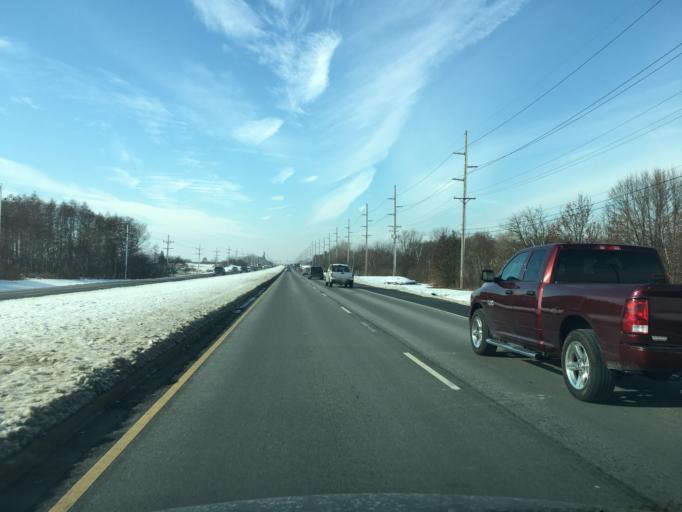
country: US
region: Illinois
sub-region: DuPage County
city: Naperville
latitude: 41.7476
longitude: -88.1758
